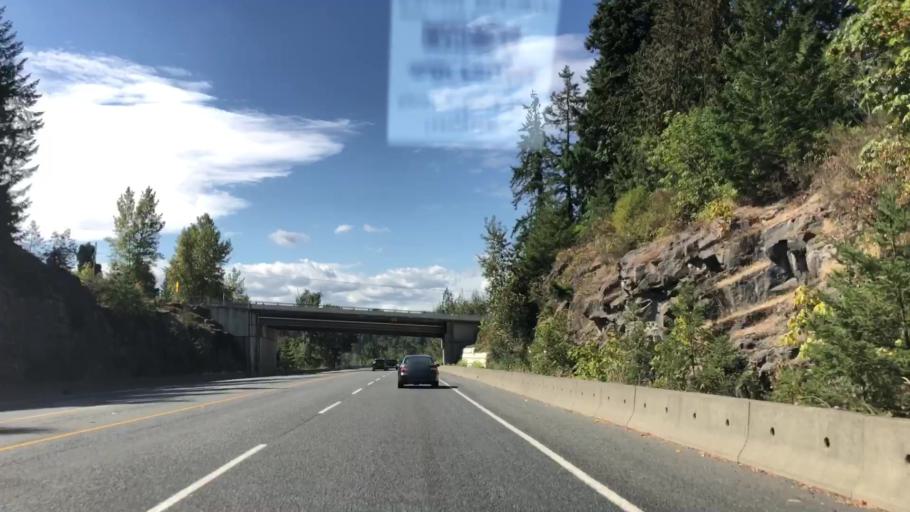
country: CA
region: British Columbia
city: Nanaimo
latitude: 49.1157
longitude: -123.8758
